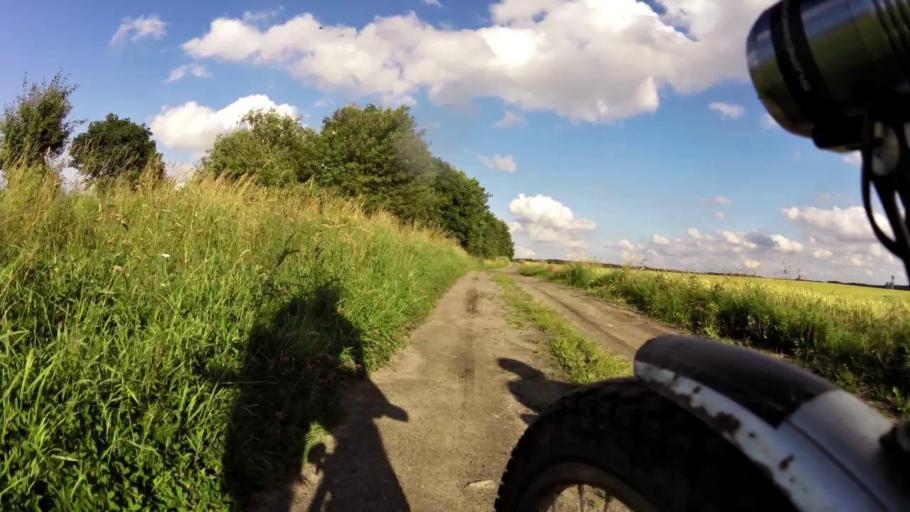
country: PL
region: West Pomeranian Voivodeship
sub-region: Powiat swidwinski
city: Swidwin
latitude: 53.7684
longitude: 15.8706
